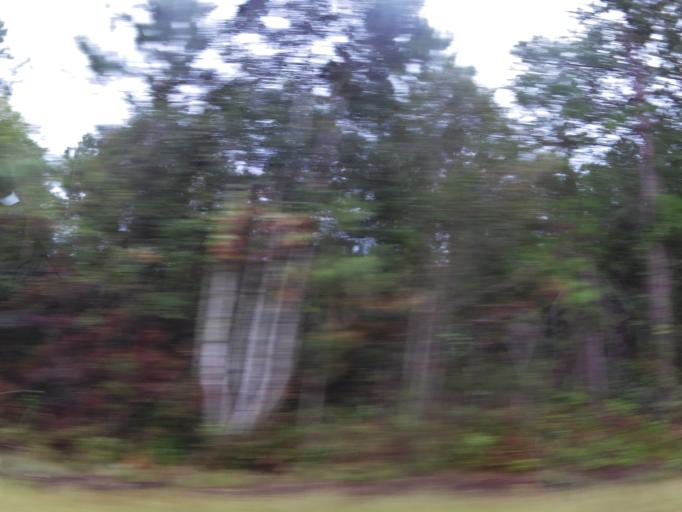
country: US
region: Georgia
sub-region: Wayne County
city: Jesup
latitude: 31.5157
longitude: -81.7726
